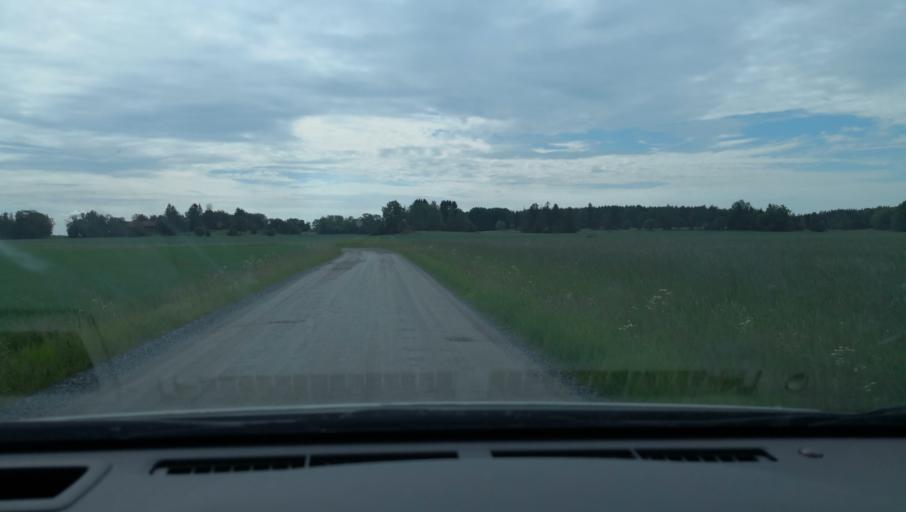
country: SE
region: Uppsala
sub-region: Enkopings Kommun
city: Enkoping
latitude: 59.7056
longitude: 17.1514
